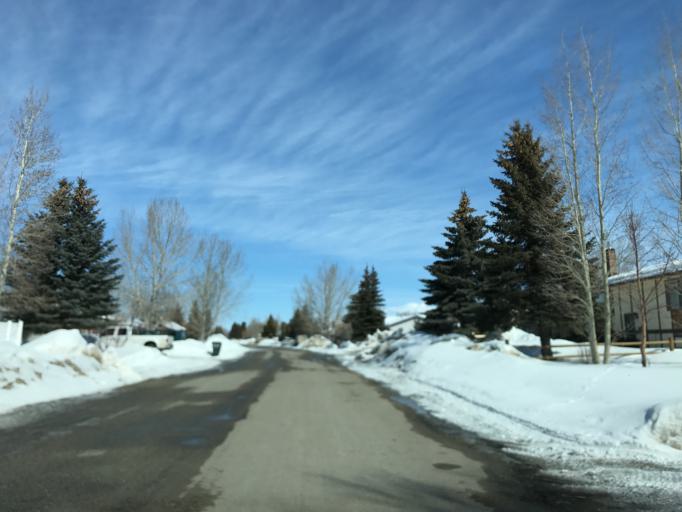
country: US
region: Wyoming
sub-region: Sublette County
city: Pinedale
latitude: 42.8594
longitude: -109.8691
